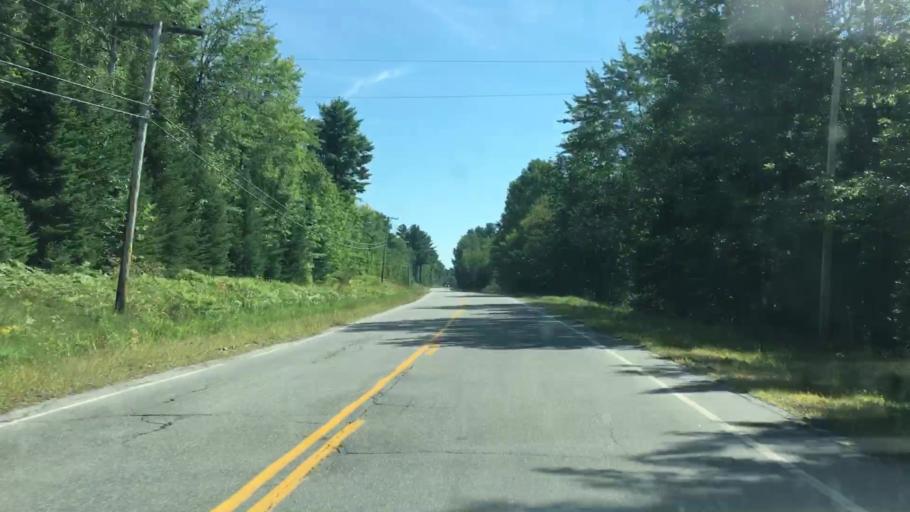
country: US
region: Maine
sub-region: Piscataquis County
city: Milo
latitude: 45.1953
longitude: -68.9024
